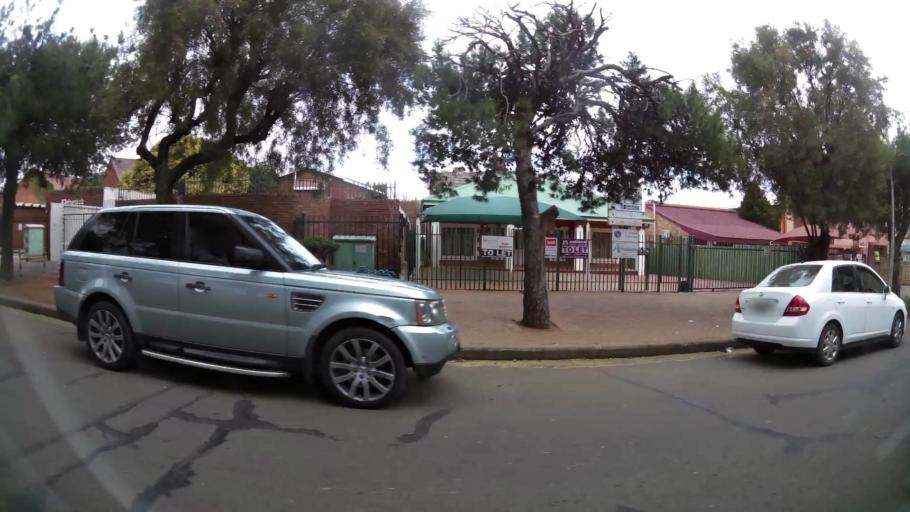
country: ZA
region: Orange Free State
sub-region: Mangaung Metropolitan Municipality
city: Bloemfontein
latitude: -29.1084
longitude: 26.2111
